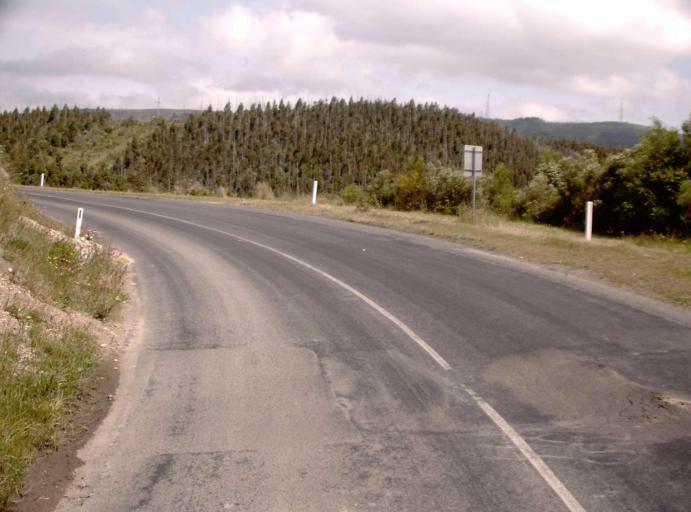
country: AU
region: Victoria
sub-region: Latrobe
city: Traralgon
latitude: -38.3660
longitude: 146.5653
